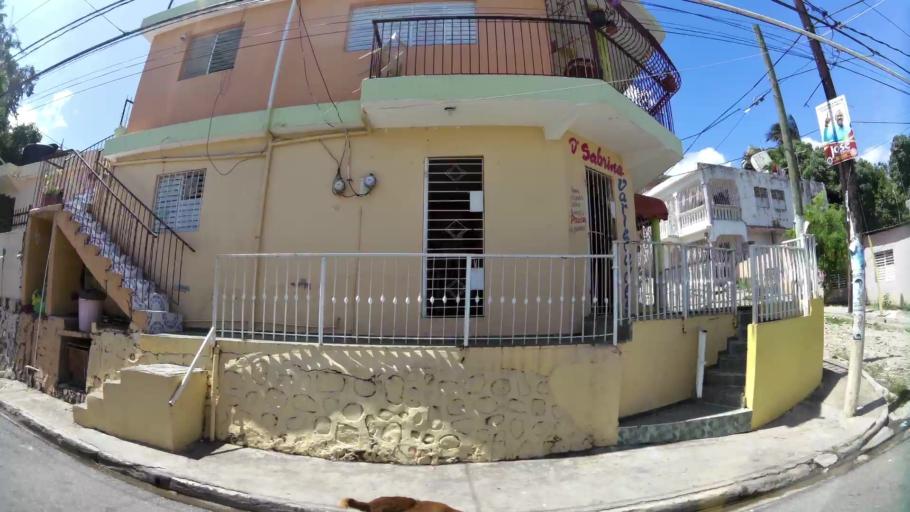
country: DO
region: San Cristobal
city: San Cristobal
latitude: 18.4046
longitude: -70.1117
